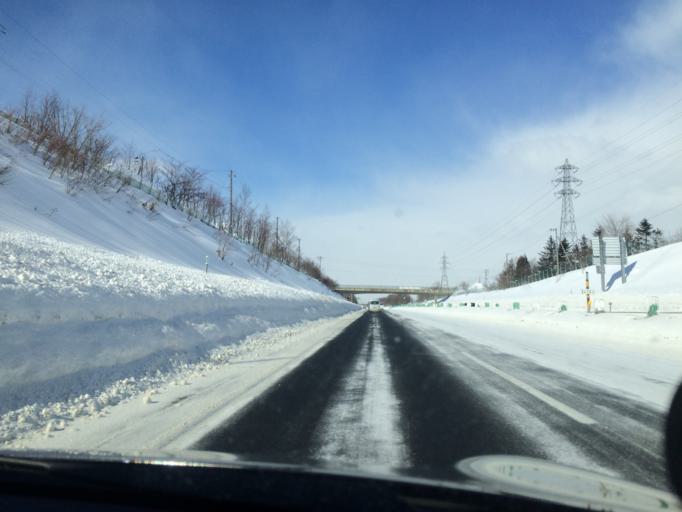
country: JP
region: Hokkaido
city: Kitahiroshima
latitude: 42.9651
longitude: 141.4946
